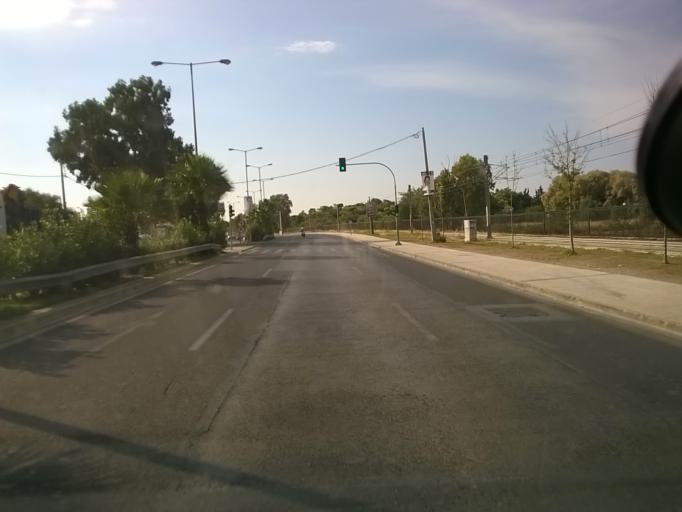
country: GR
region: Attica
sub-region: Nomarchia Athinas
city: Alimos
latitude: 37.9011
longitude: 23.7197
